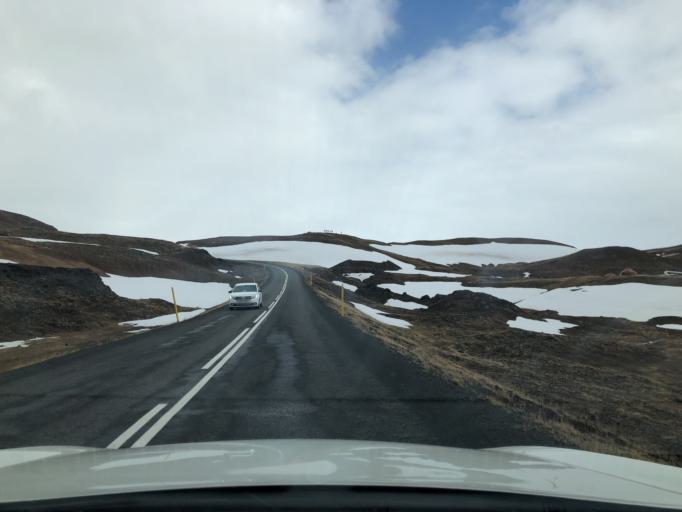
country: IS
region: Northeast
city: Laugar
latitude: 65.7072
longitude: -16.7716
